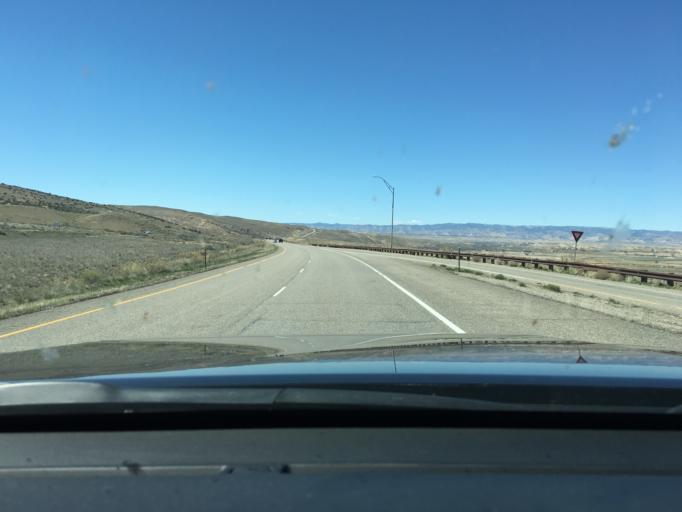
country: US
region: Colorado
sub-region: Mesa County
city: Loma
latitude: 39.2159
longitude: -108.8703
